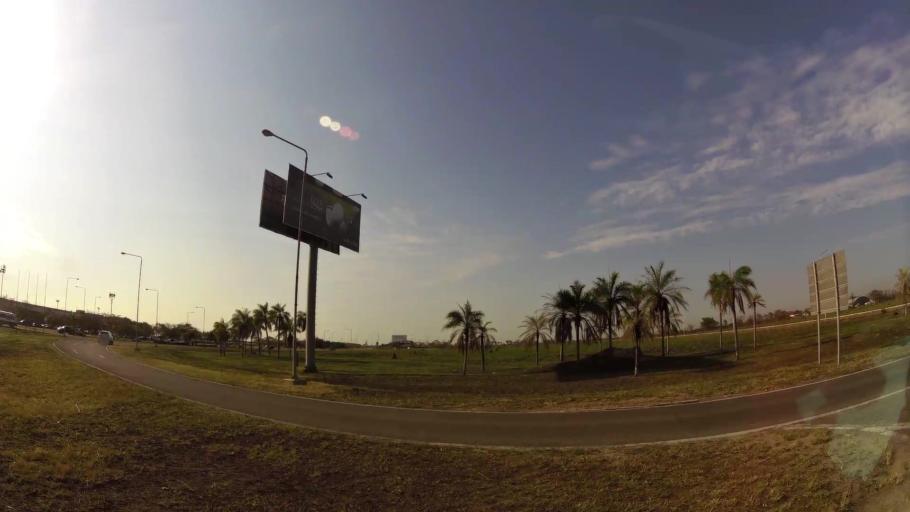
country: BO
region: Santa Cruz
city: La Belgica
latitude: -17.6488
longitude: -63.1429
